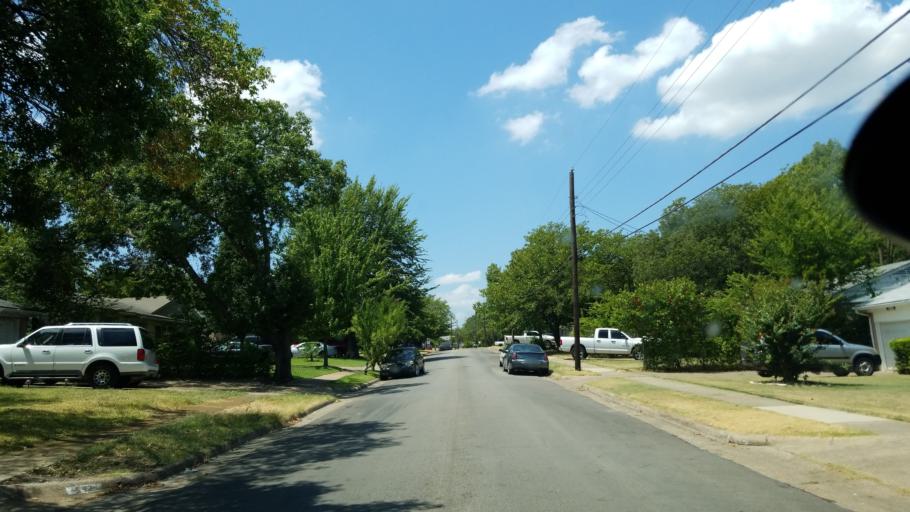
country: US
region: Texas
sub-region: Dallas County
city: Duncanville
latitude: 32.6684
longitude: -96.8985
